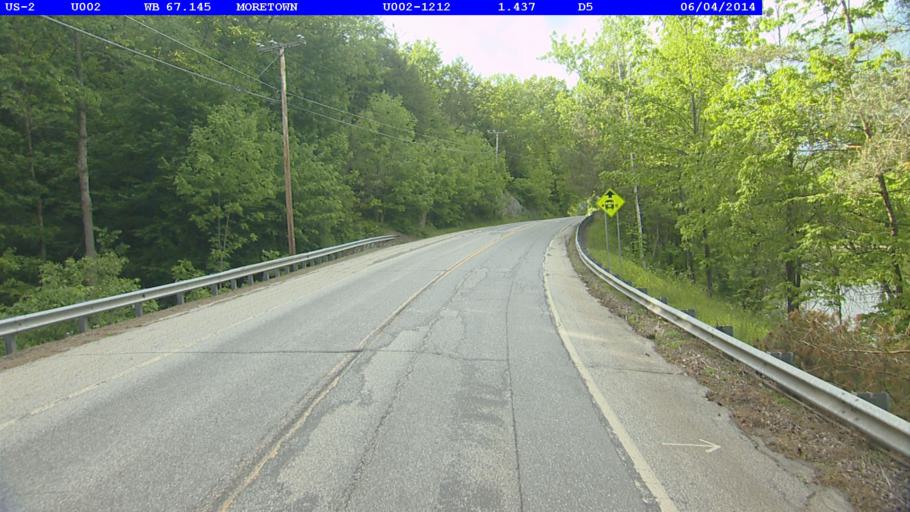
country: US
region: Vermont
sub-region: Washington County
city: Waterbury
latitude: 44.3141
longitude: -72.7250
